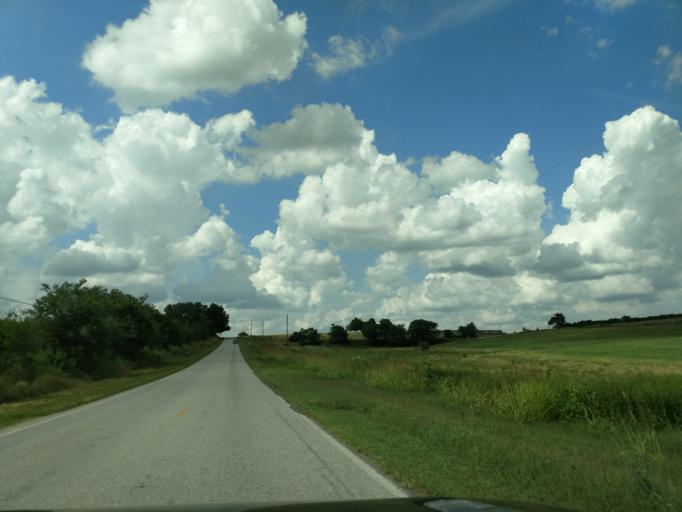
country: US
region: Arkansas
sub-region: Carroll County
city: Berryville
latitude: 36.4266
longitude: -93.5564
